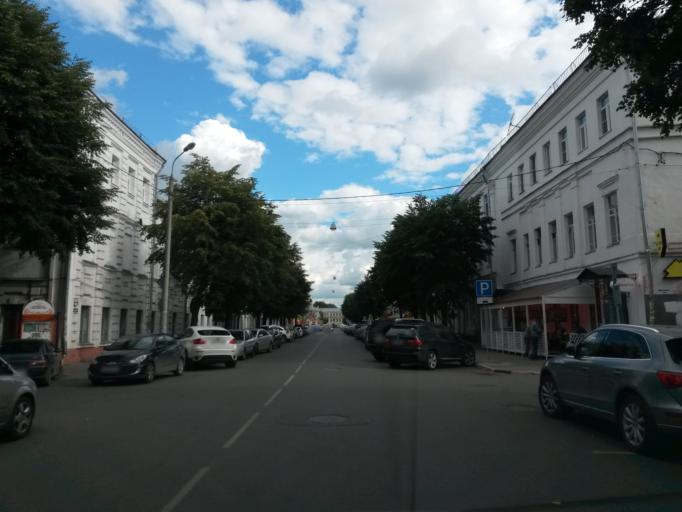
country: RU
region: Jaroslavl
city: Yaroslavl
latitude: 57.6270
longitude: 39.8886
